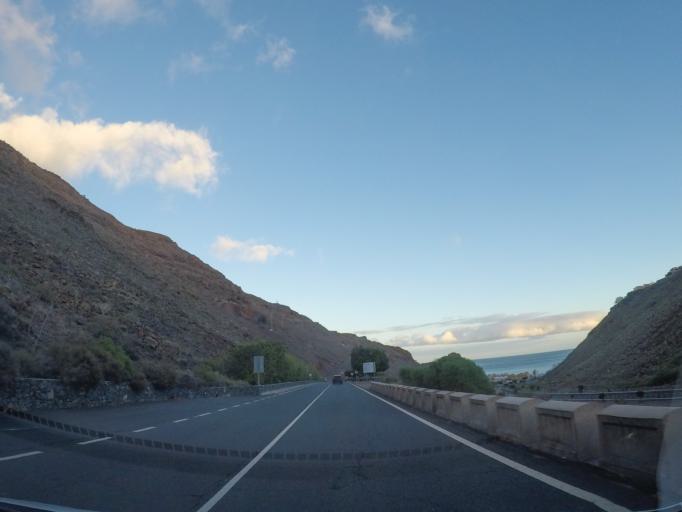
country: ES
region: Canary Islands
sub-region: Provincia de Santa Cruz de Tenerife
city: Alajero
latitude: 28.0346
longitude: -17.2050
